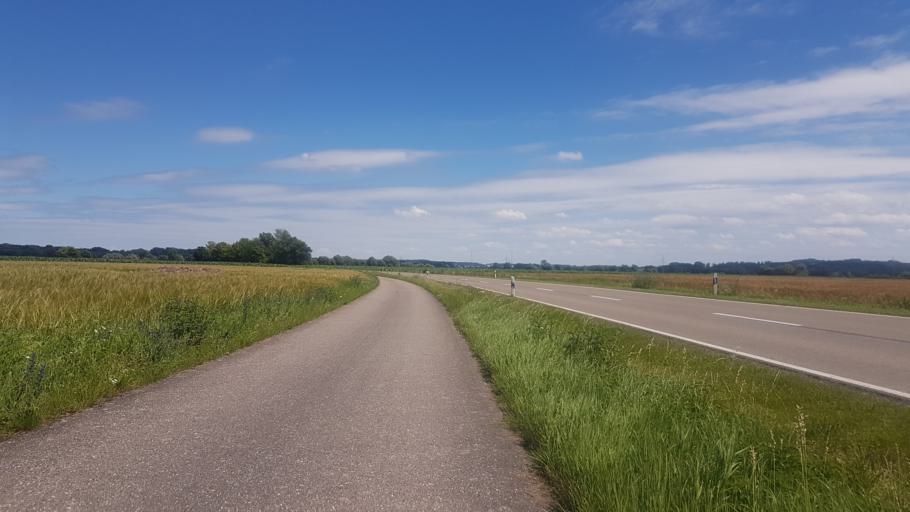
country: DE
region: Bavaria
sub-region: Swabia
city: Schwenningen
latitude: 48.6288
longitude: 10.6566
